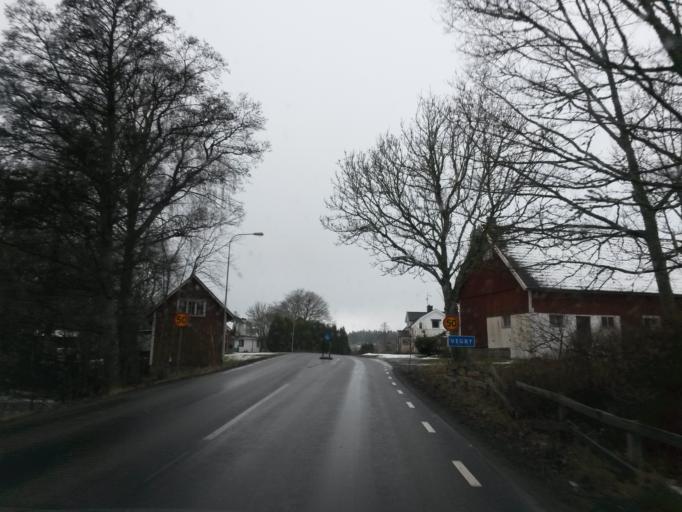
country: SE
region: Vaestra Goetaland
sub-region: Ulricehamns Kommun
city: Ulricehamn
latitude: 57.6783
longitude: 13.3884
